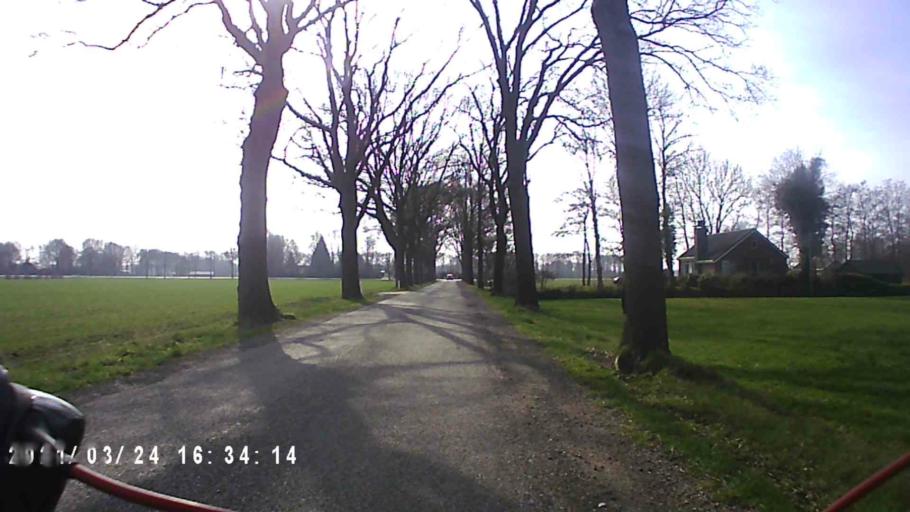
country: NL
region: Groningen
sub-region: Gemeente Leek
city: Leek
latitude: 53.0685
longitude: 6.2741
